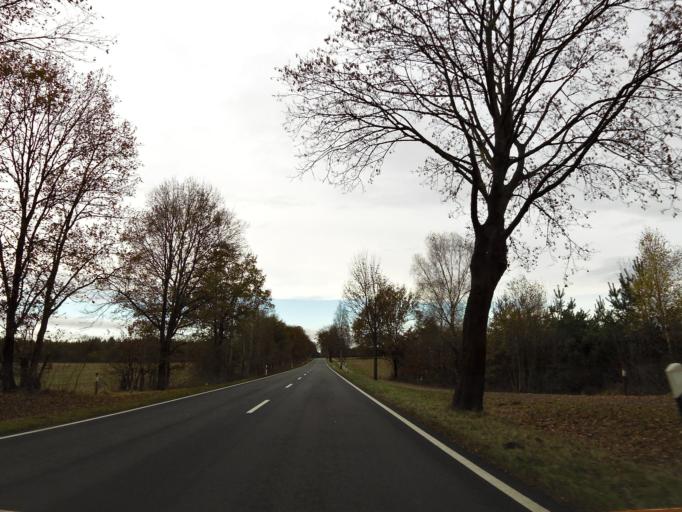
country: DE
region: Lower Saxony
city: Eimke
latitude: 52.9708
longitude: 10.2761
